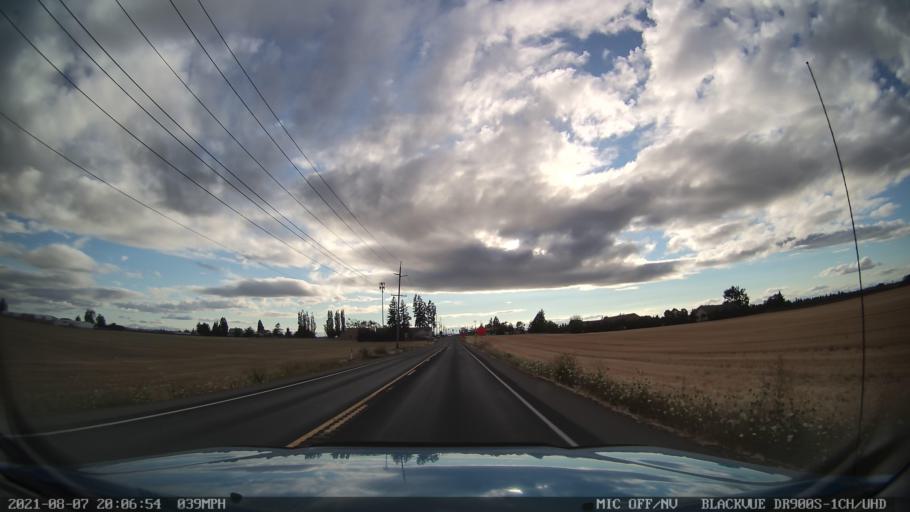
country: US
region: Oregon
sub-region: Marion County
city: Silverton
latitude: 44.9914
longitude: -122.8748
